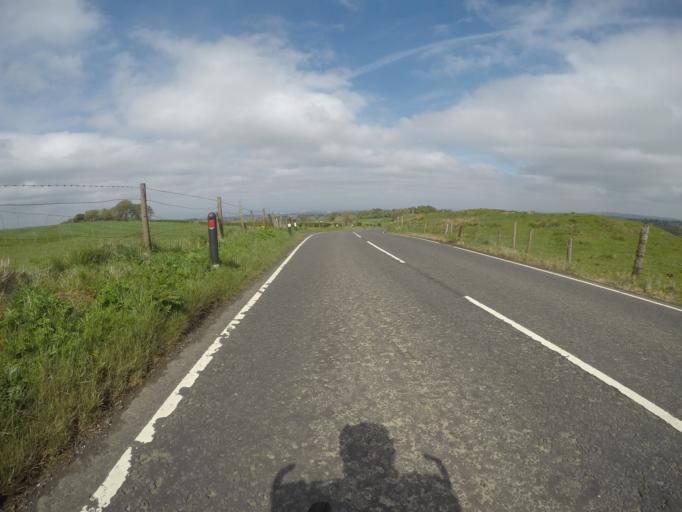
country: GB
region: Scotland
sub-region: East Renfrewshire
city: Newton Mearns
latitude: 55.7727
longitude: -4.3678
